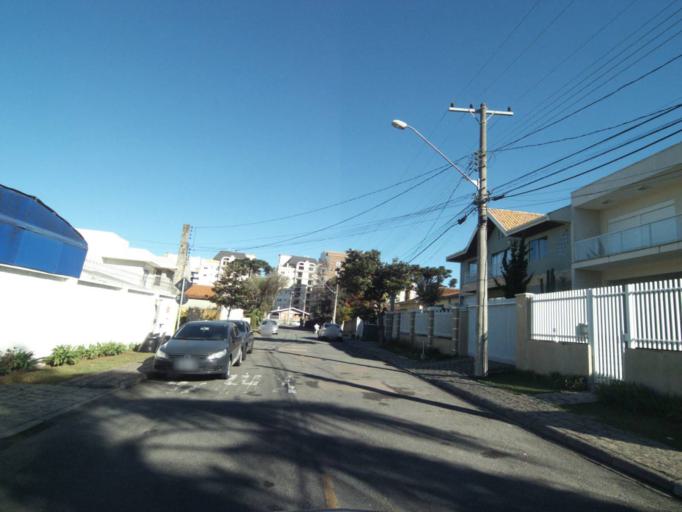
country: BR
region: Parana
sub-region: Curitiba
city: Curitiba
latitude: -25.3989
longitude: -49.2553
